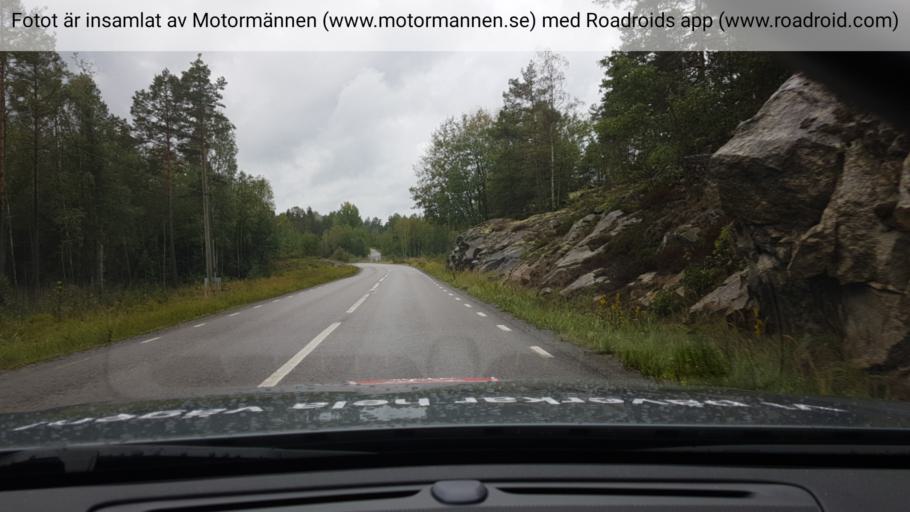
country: SE
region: Stockholm
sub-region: Botkyrka Kommun
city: Tullinge
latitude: 59.1861
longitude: 17.9281
